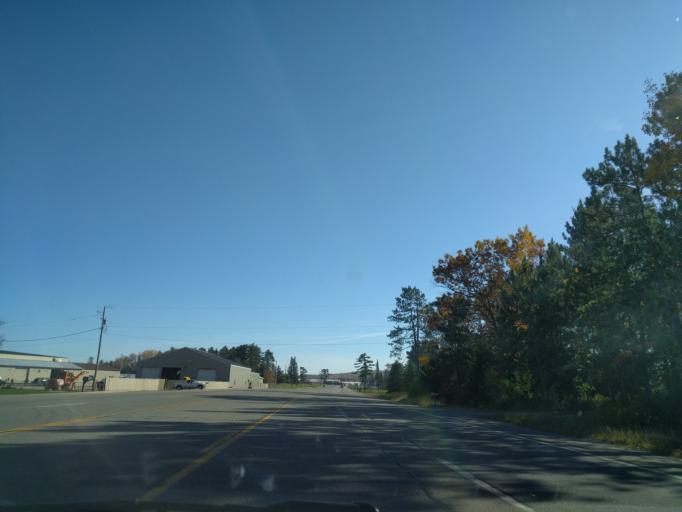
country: US
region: Michigan
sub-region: Dickinson County
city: Iron Mountain
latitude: 45.8513
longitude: -88.0534
